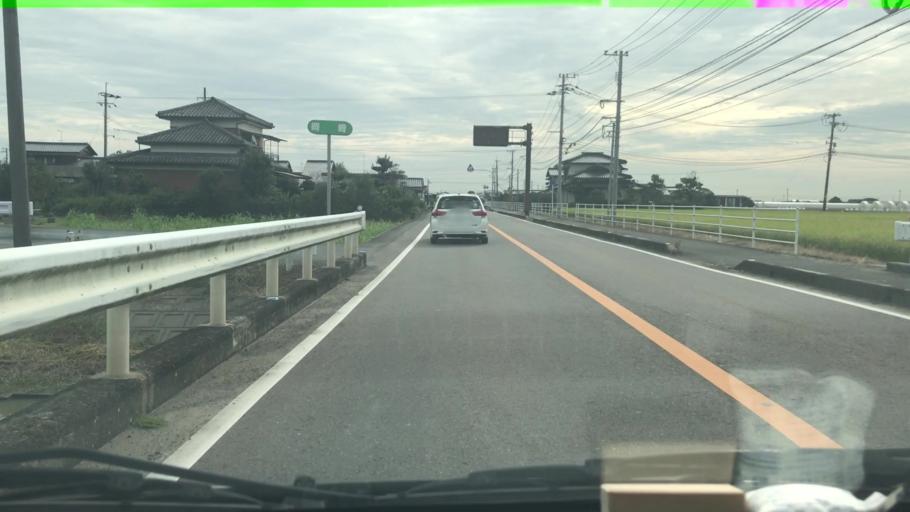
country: JP
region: Saga Prefecture
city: Takeocho-takeo
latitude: 33.1981
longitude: 130.1042
